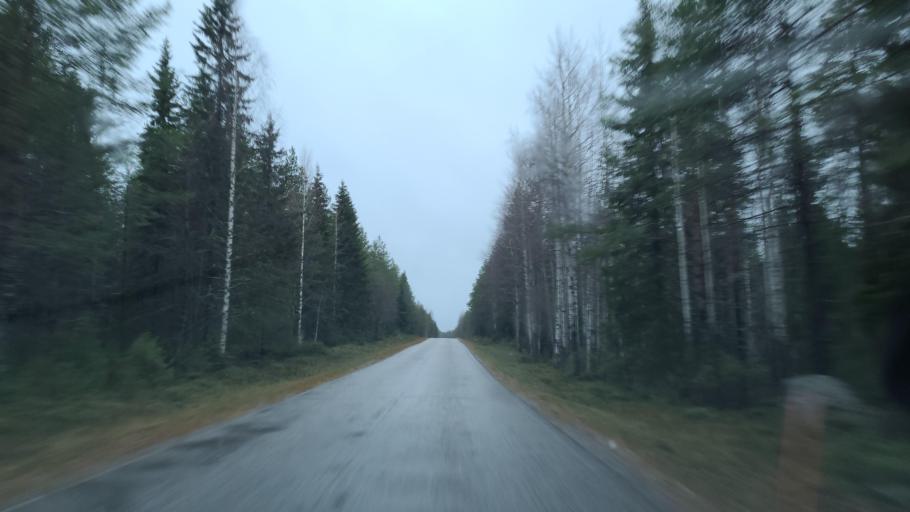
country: FI
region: Lapland
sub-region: Kemi-Tornio
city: Simo
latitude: 65.8751
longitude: 25.2223
